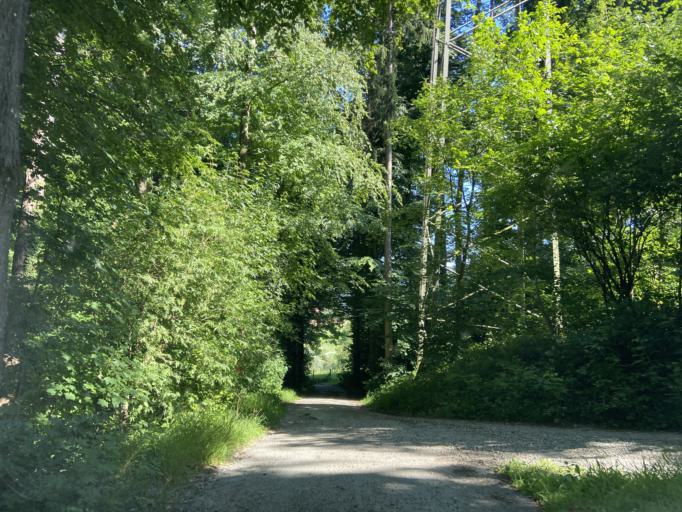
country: CH
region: Zurich
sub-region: Bezirk Winterthur
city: Wuelflingen (Kreis 6) / Niederfeld
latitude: 47.5032
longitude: 8.6684
